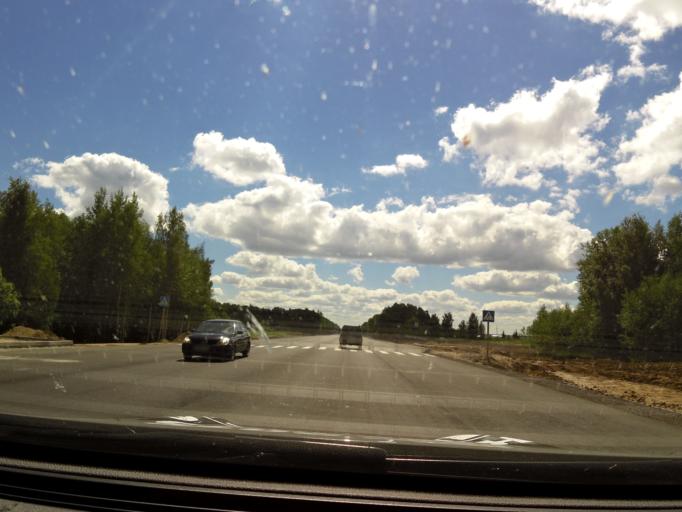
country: RU
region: Vologda
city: Molochnoye
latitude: 59.3239
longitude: 39.6830
